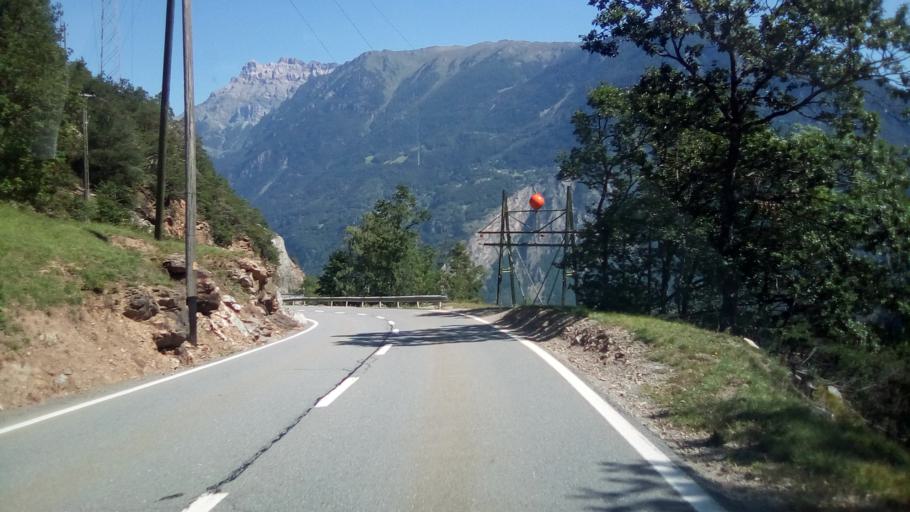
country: CH
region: Valais
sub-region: Saint-Maurice District
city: Vernayaz
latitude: 46.1230
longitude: 7.0323
